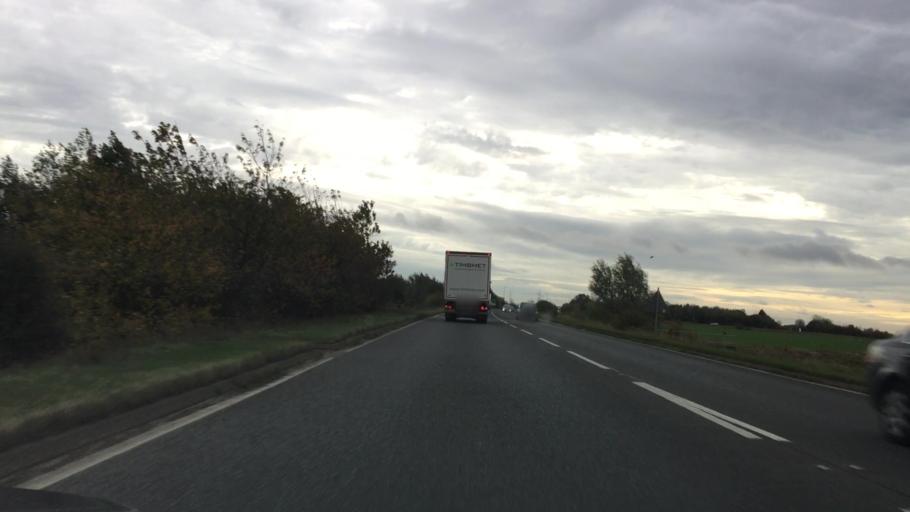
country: GB
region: England
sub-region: Lincolnshire
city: Gosberton
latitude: 52.9017
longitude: -0.1142
